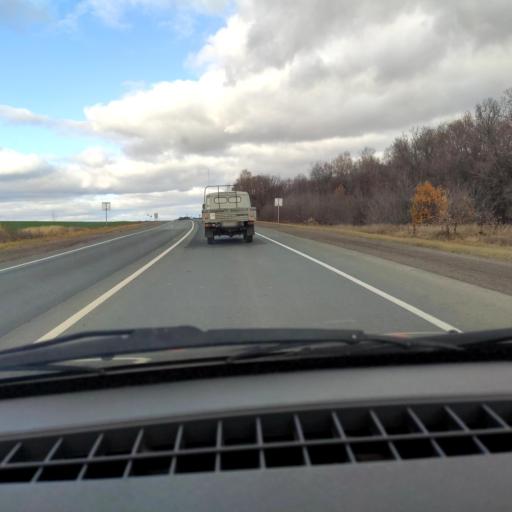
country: RU
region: Bashkortostan
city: Avdon
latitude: 54.7372
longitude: 55.7835
